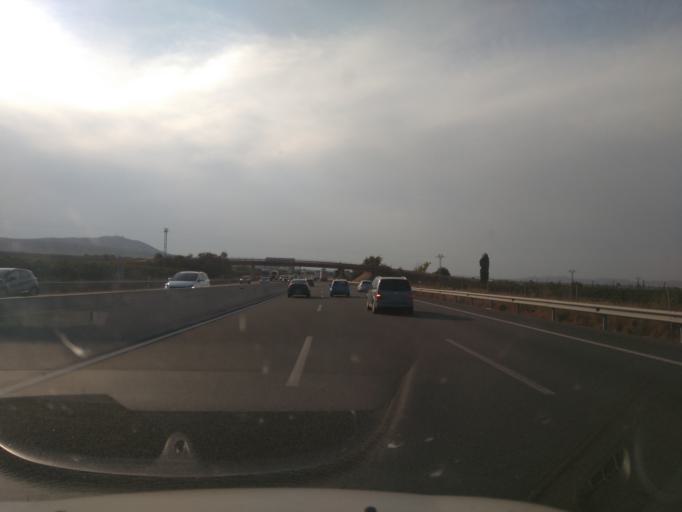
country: ES
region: Valencia
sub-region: Provincia de Valencia
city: Torrent
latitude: 39.4219
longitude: -0.5163
